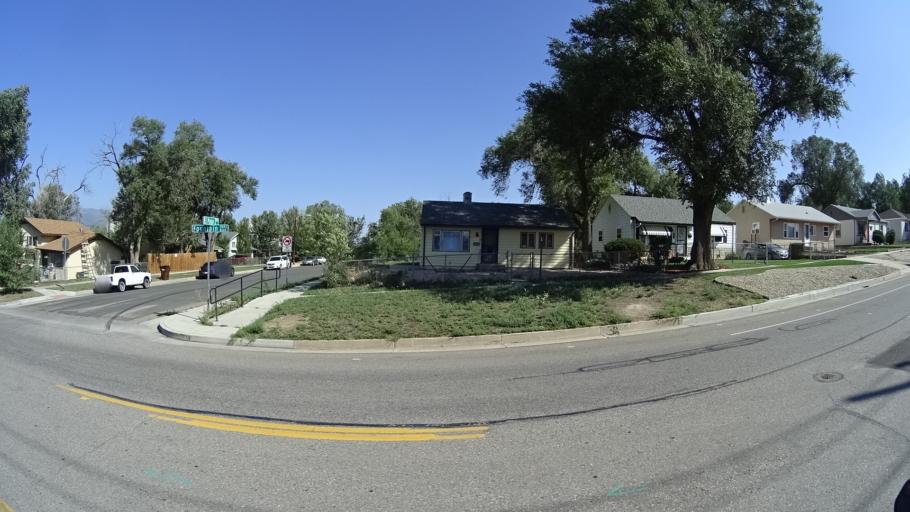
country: US
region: Colorado
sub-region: El Paso County
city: Colorado Springs
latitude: 38.8214
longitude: -104.8133
